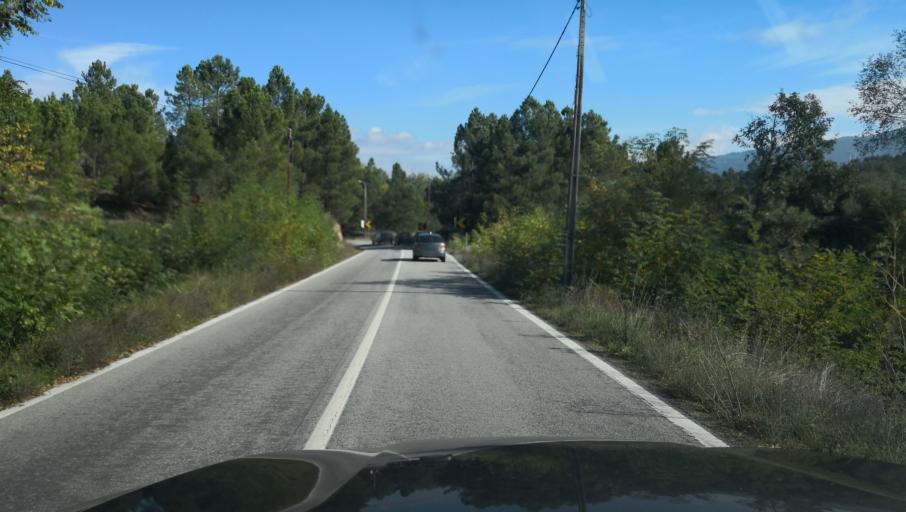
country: PT
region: Vila Real
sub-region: Chaves
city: Chaves
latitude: 41.7204
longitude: -7.4903
